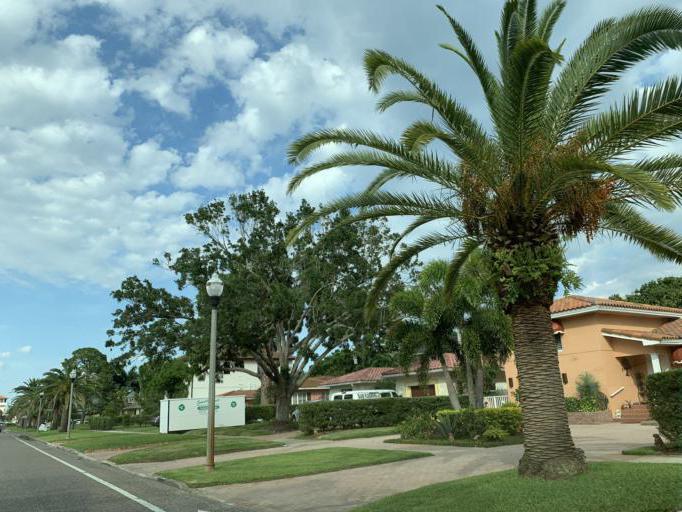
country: US
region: Florida
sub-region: Pinellas County
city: Saint Petersburg
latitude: 27.7944
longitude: -82.6240
